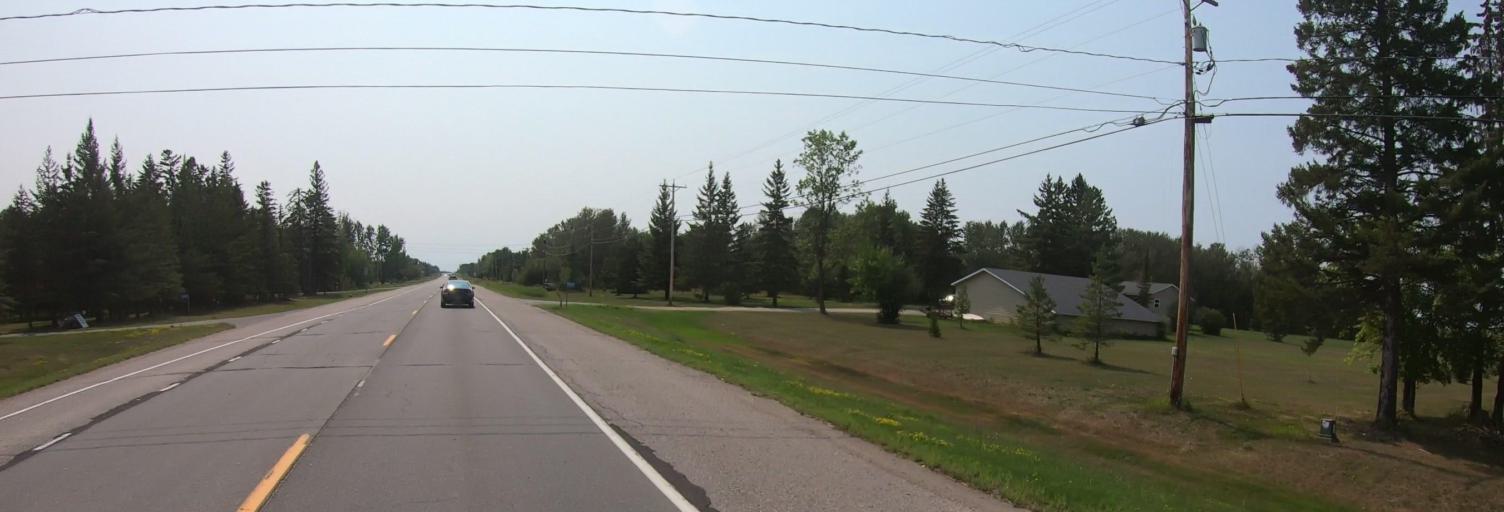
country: US
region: Minnesota
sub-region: Koochiching County
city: International Falls
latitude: 48.5813
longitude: -93.4402
